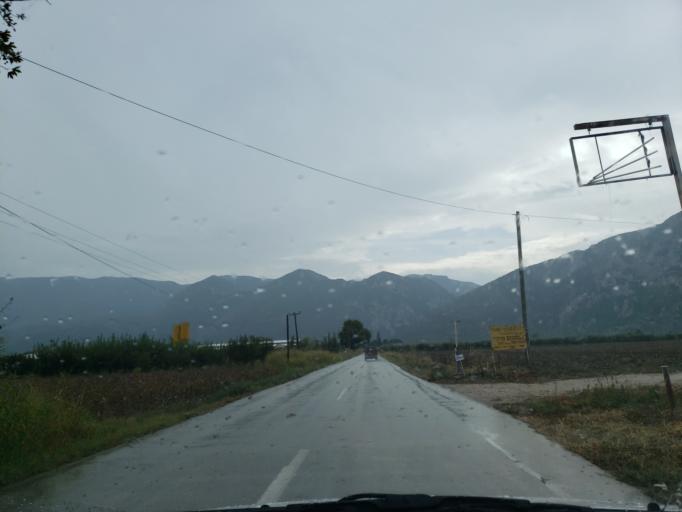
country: GR
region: Central Greece
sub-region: Nomos Fthiotidos
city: Anthili
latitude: 38.8105
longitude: 22.4424
